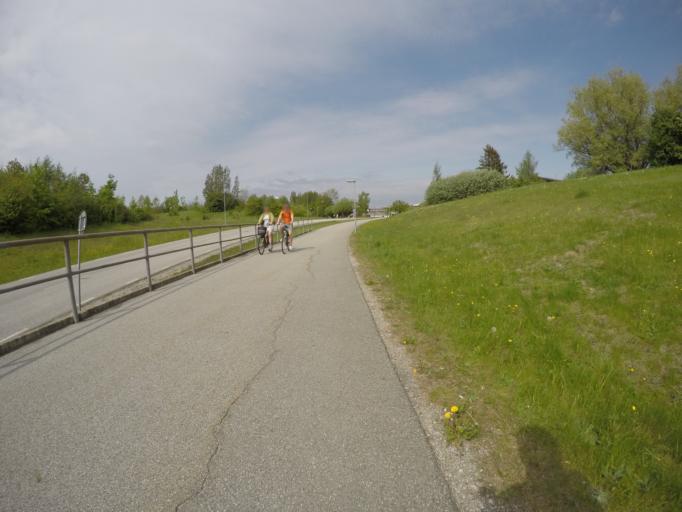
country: SE
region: Skane
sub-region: Malmo
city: Tygelsjo
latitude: 55.5544
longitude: 12.9912
